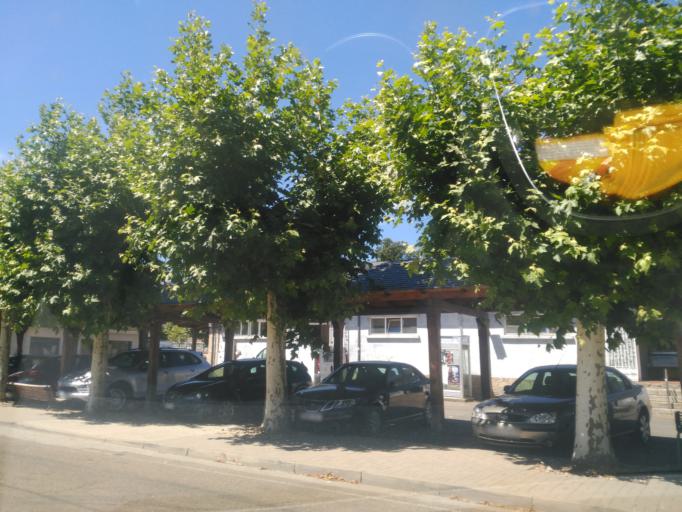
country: ES
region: Castille and Leon
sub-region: Provincia de Zamora
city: Galende
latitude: 42.0846
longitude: -6.6408
